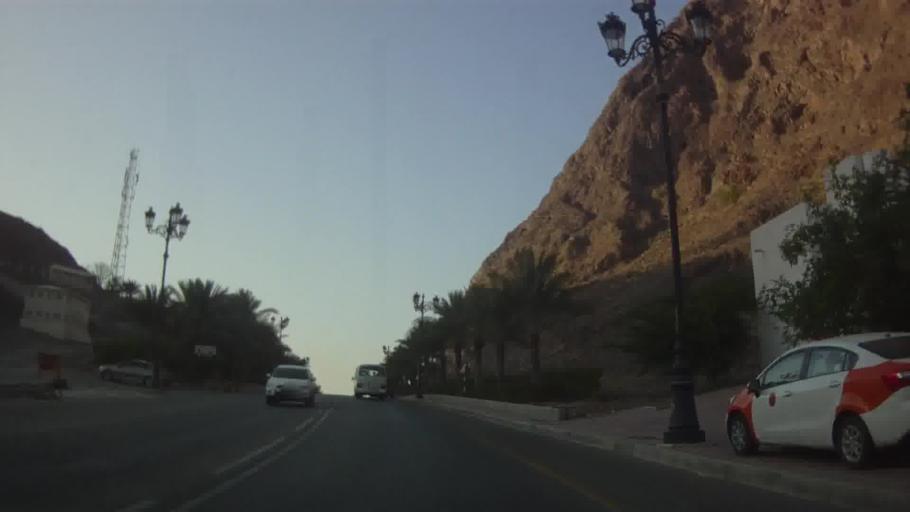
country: OM
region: Muhafazat Masqat
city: Muscat
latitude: 23.6067
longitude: 58.5971
